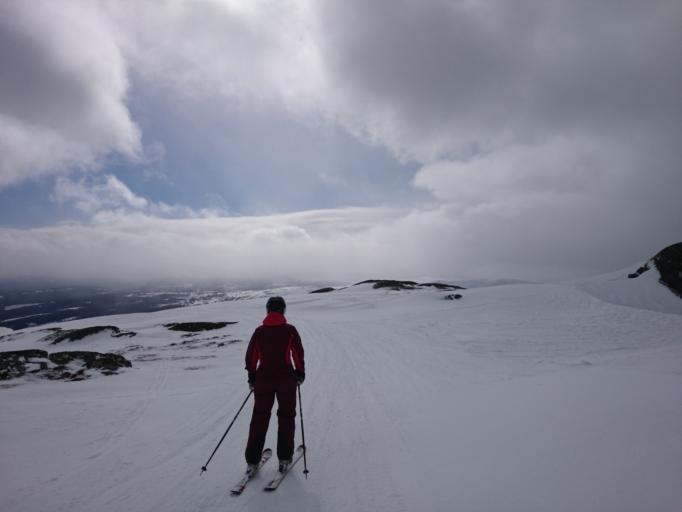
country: SE
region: Jaemtland
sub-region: Are Kommun
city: Are
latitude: 63.4143
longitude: 13.0808
